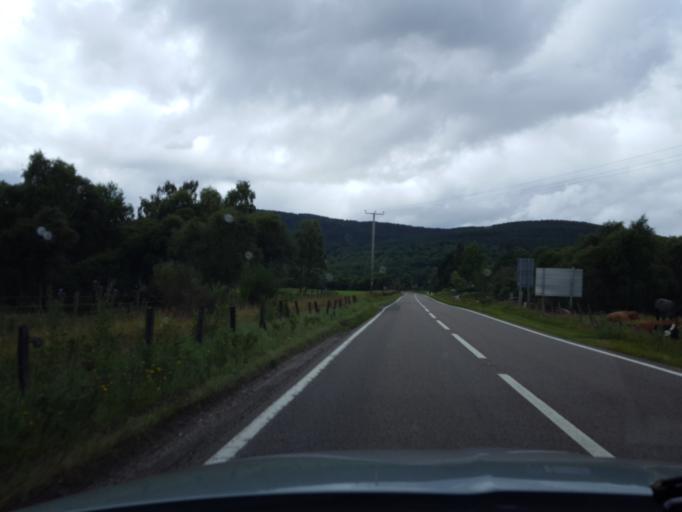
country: GB
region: Scotland
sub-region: Highland
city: Aviemore
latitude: 57.2498
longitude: -3.7906
